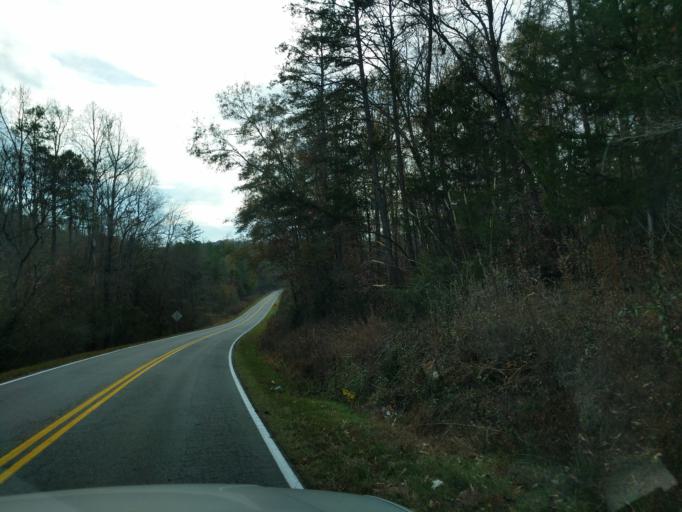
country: US
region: South Carolina
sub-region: Pickens County
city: Clemson
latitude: 34.7898
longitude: -82.8868
